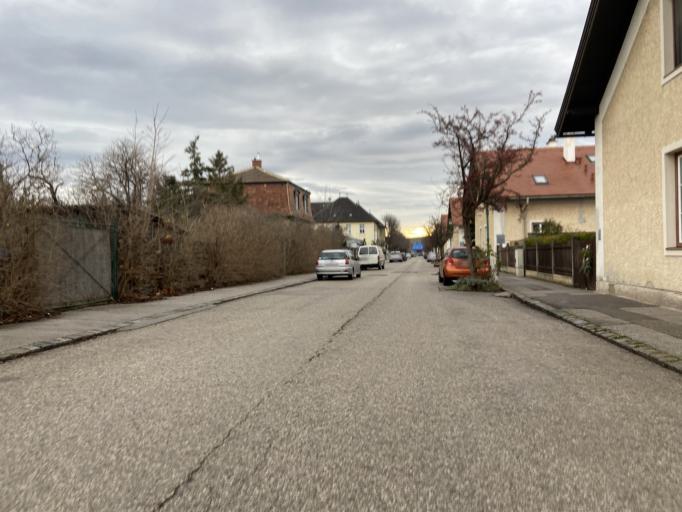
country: AT
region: Lower Austria
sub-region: Politischer Bezirk Modling
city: Wiener Neudorf
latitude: 48.0799
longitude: 16.3045
